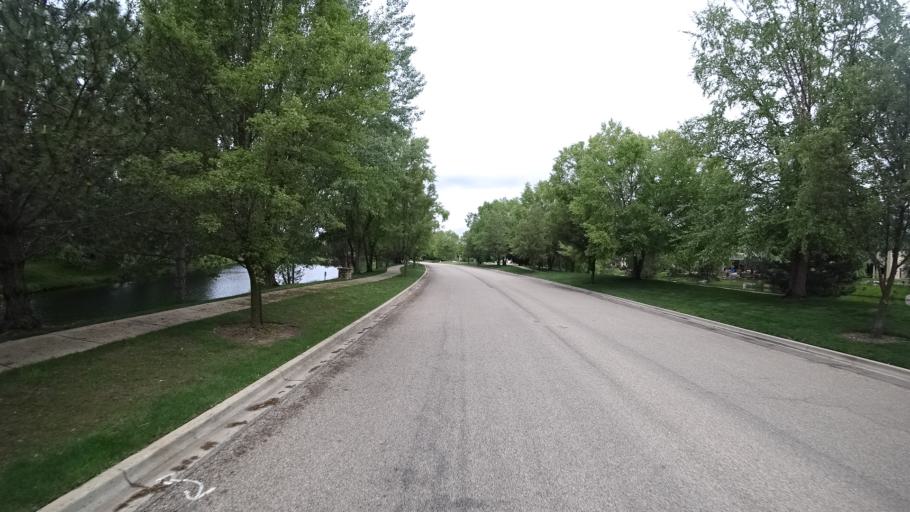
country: US
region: Idaho
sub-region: Ada County
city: Eagle
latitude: 43.6790
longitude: -116.3396
